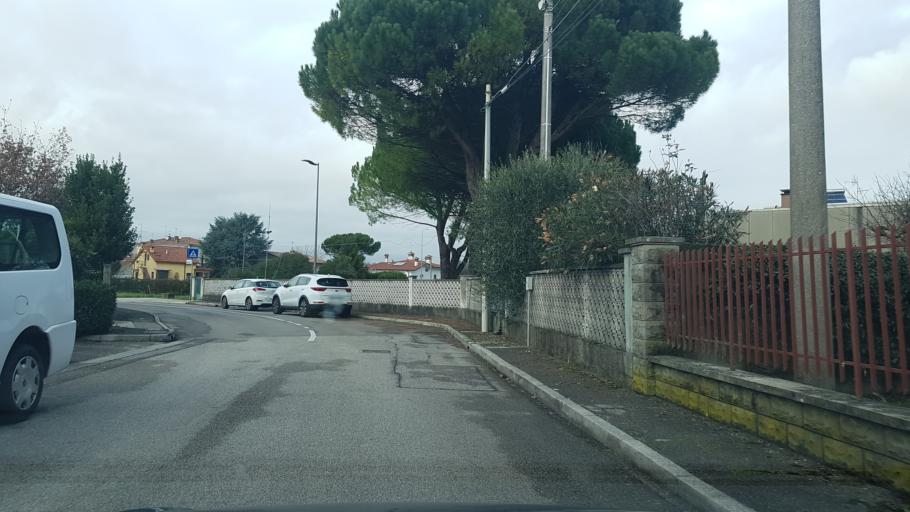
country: IT
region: Friuli Venezia Giulia
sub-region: Provincia di Gorizia
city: San Lorenzo Isontino
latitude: 45.9322
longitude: 13.5301
